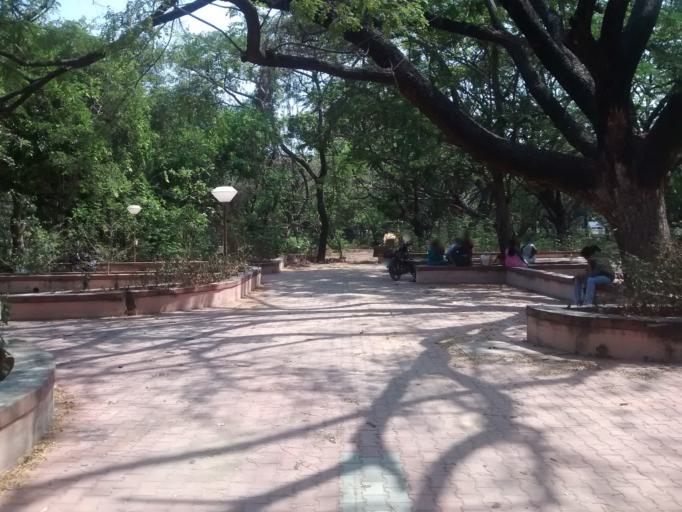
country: IN
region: Tamil Nadu
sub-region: Chennai
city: Gandhi Nagar
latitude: 13.0106
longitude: 80.2347
